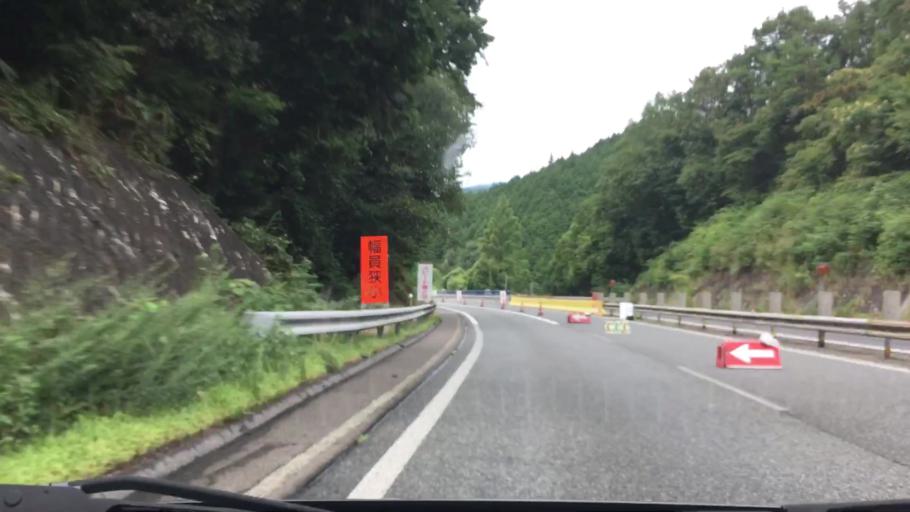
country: JP
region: Okayama
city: Niimi
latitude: 35.0189
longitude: 133.5831
